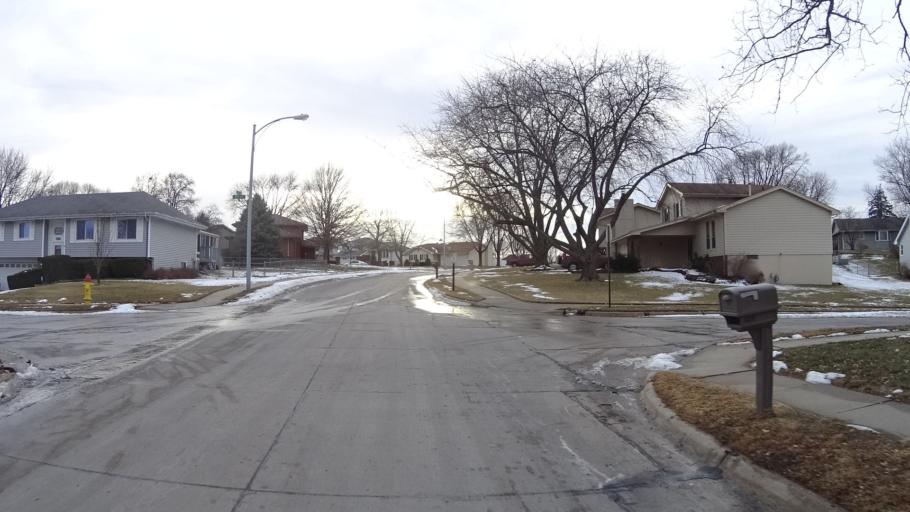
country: US
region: Nebraska
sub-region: Sarpy County
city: Offutt Air Force Base
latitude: 41.1650
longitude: -95.9461
